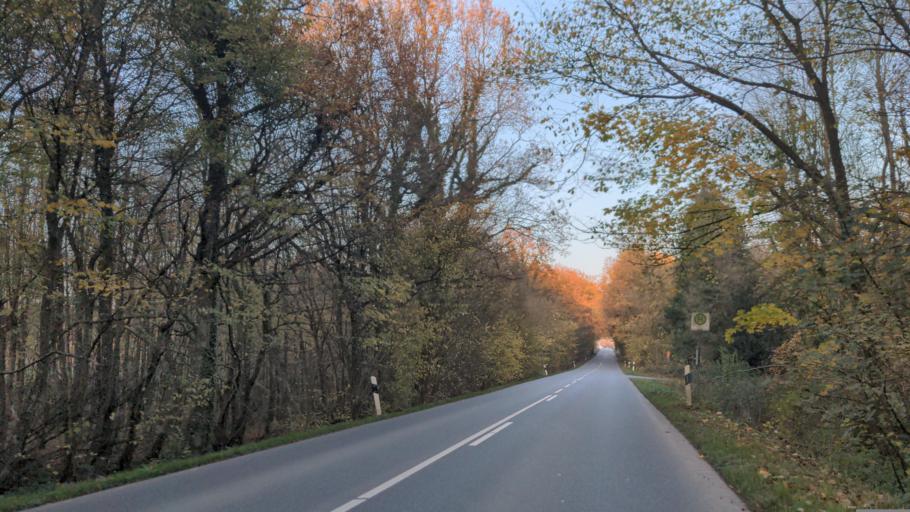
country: DE
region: Schleswig-Holstein
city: Glasau
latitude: 54.0994
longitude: 10.5215
